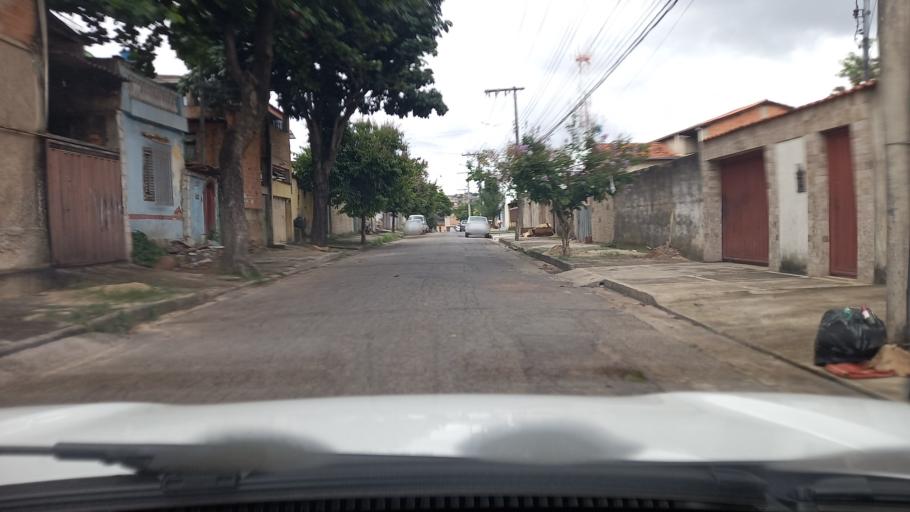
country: BR
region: Minas Gerais
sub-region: Contagem
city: Contagem
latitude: -19.8977
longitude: -44.0138
